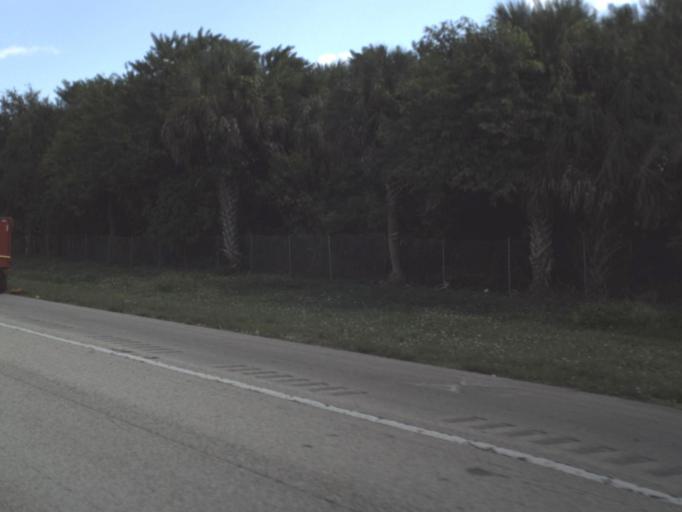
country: US
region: Florida
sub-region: Palm Beach County
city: Plantation Mobile Home Park
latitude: 26.7068
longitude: -80.1418
